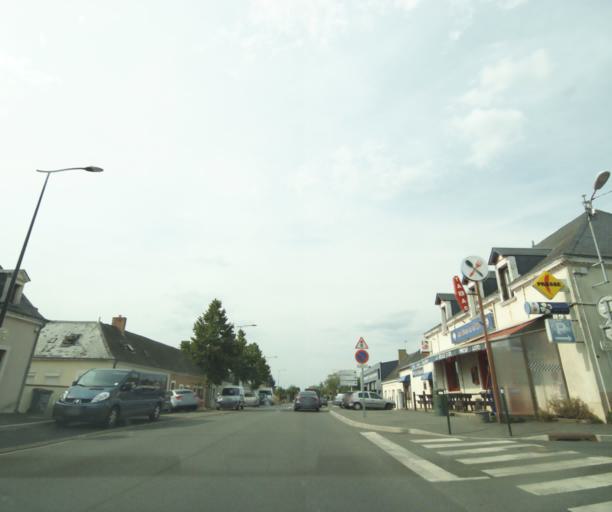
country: FR
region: Pays de la Loire
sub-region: Departement de la Sarthe
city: Mulsanne
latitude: 47.9055
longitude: 0.2447
